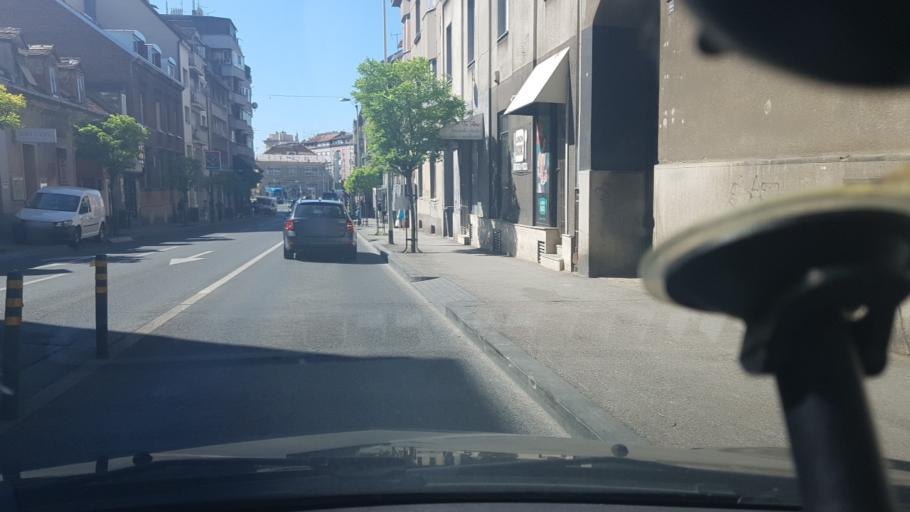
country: HR
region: Grad Zagreb
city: Zagreb
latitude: 45.8163
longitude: 15.9968
